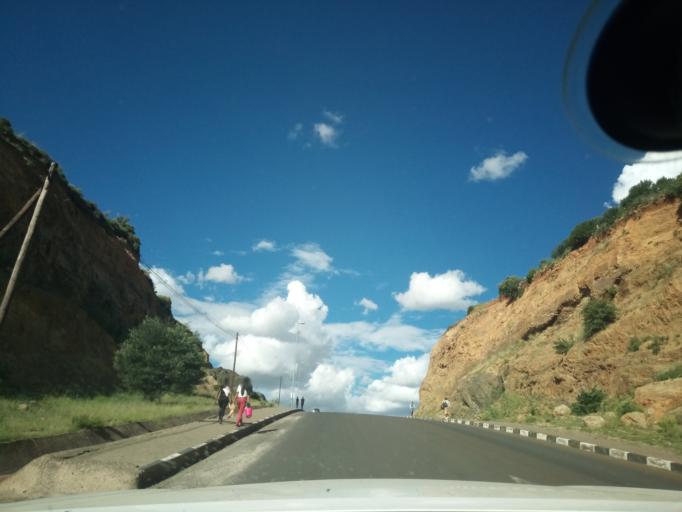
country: LS
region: Maseru
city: Maseru
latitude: -29.3300
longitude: 27.4928
